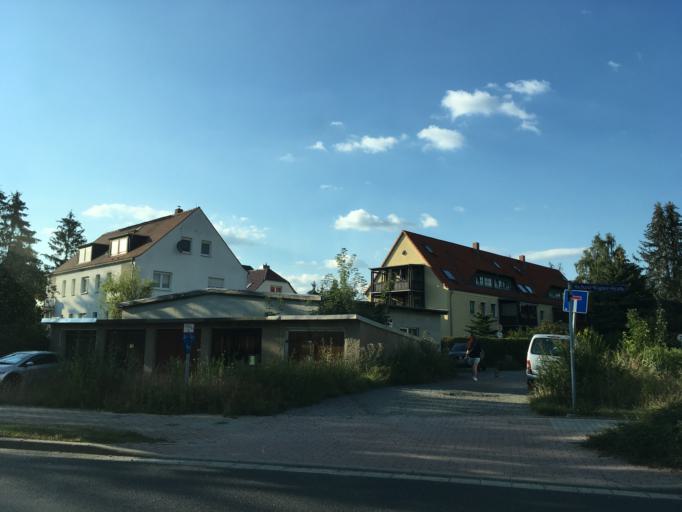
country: DE
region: Saxony
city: Radeberg
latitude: 51.1064
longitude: 13.9182
